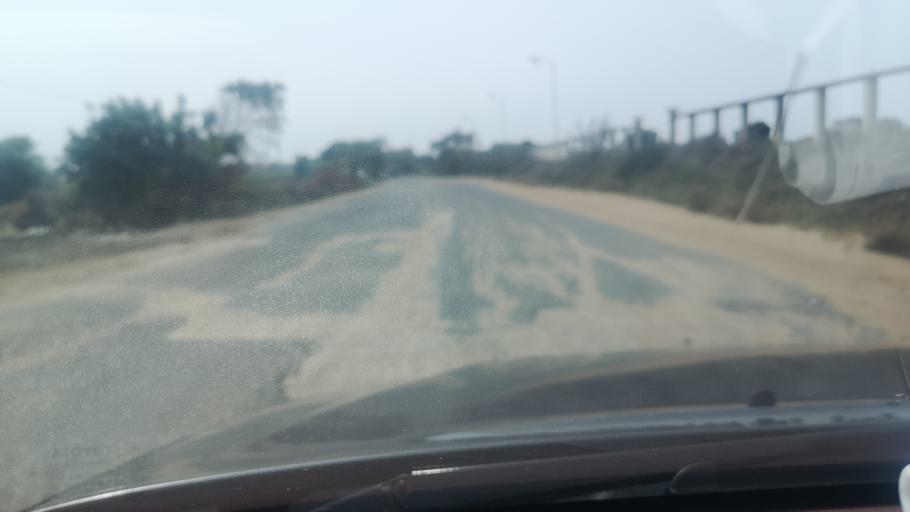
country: GH
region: Greater Accra
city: Nungua
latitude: 5.6133
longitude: -0.0562
